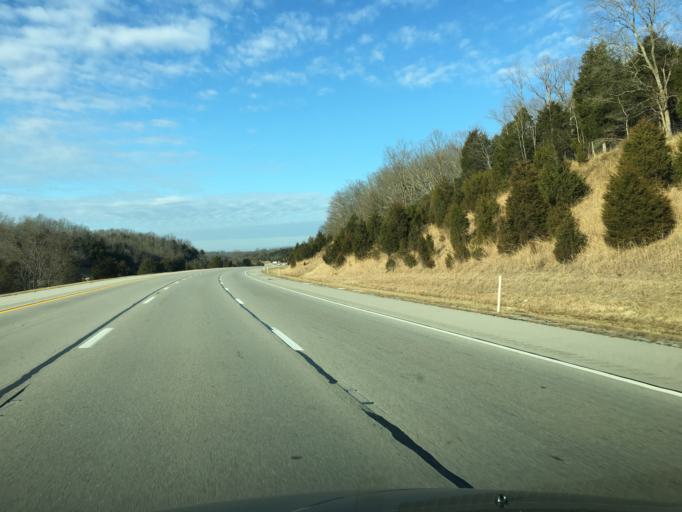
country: US
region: Kentucky
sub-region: Scott County
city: Georgetown
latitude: 38.3266
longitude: -84.5617
